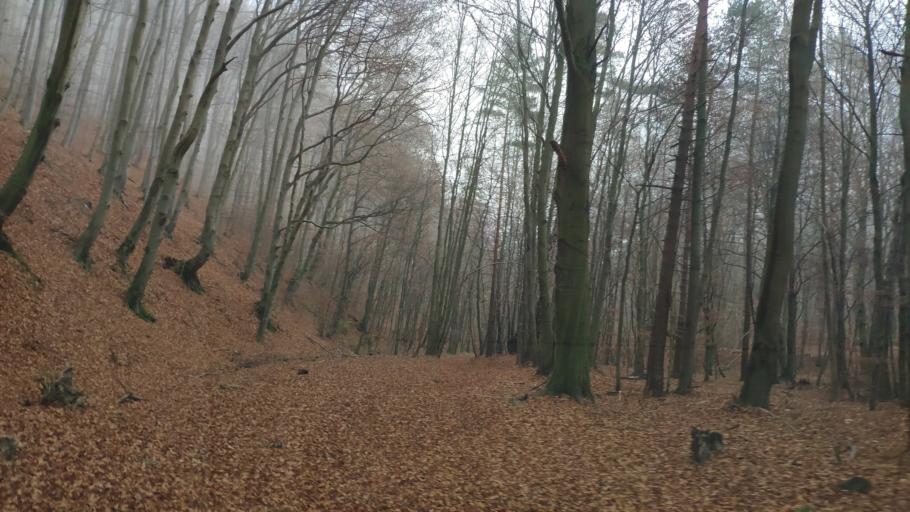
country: SK
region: Presovsky
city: Sabinov
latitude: 49.1505
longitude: 21.2078
